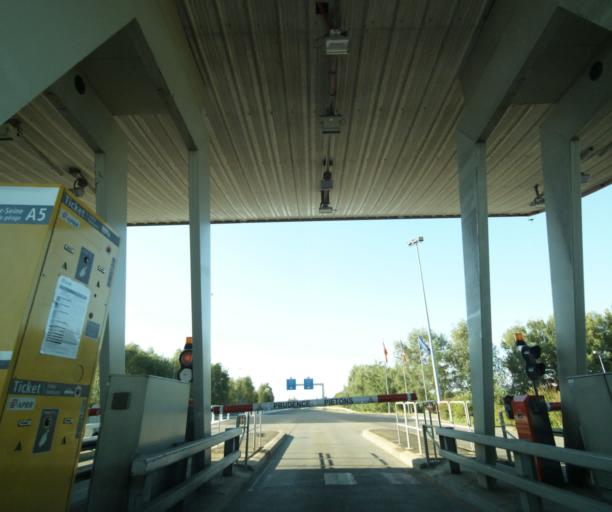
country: FR
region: Ile-de-France
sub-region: Departement de Seine-et-Marne
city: Marolles-sur-Seine
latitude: 48.3802
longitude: 3.0202
